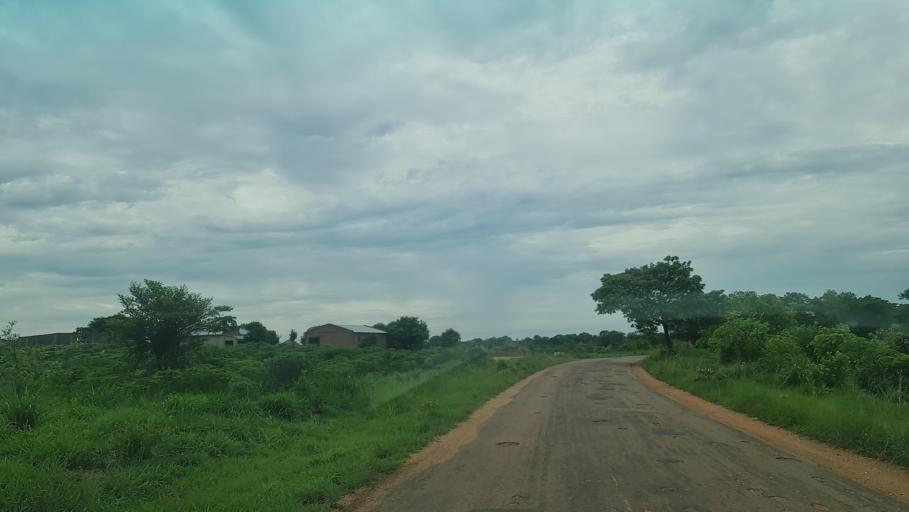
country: MW
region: Southern Region
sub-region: Nsanje District
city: Nsanje
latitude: -17.6899
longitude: 35.7330
